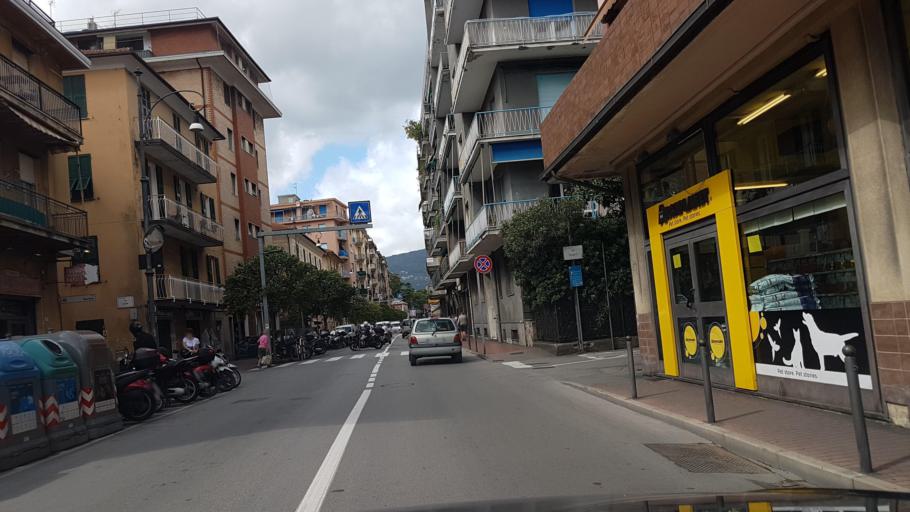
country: IT
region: Liguria
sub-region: Provincia di Genova
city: Rapallo
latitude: 44.3521
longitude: 9.2217
